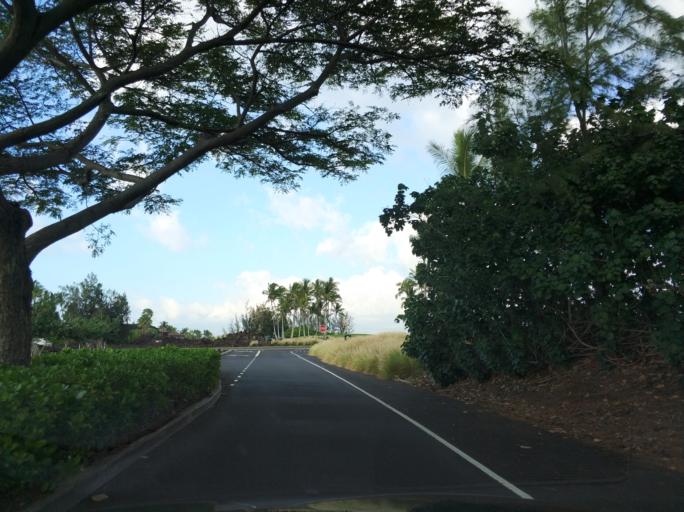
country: US
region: Hawaii
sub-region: Hawaii County
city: Waikoloa Village
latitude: 19.9217
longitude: -155.8764
